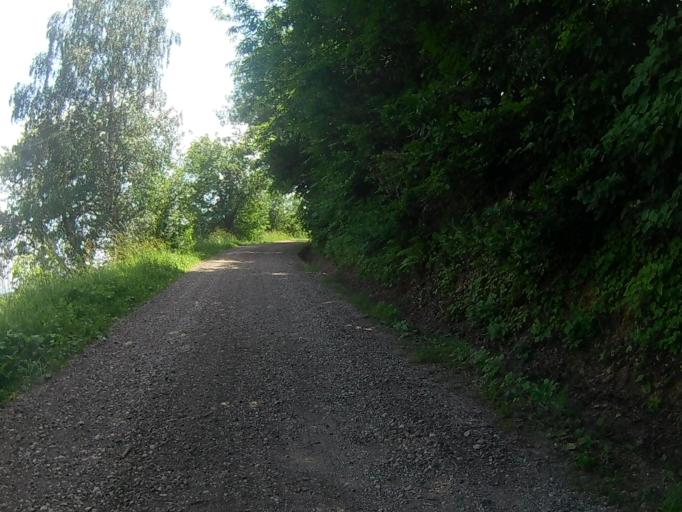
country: SI
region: Kungota
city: Zgornja Kungota
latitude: 46.6139
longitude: 15.5958
